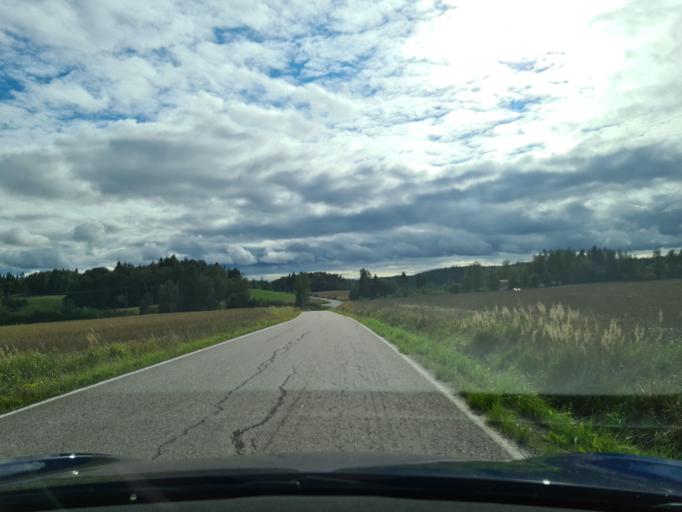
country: FI
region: Uusimaa
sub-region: Helsinki
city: Vihti
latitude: 60.4411
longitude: 24.3886
